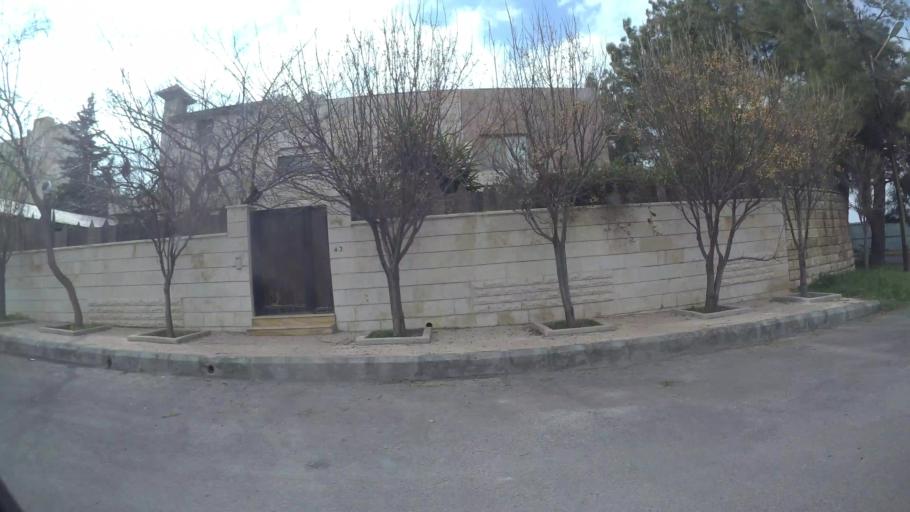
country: JO
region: Amman
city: Al Jubayhah
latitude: 32.0343
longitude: 35.8199
